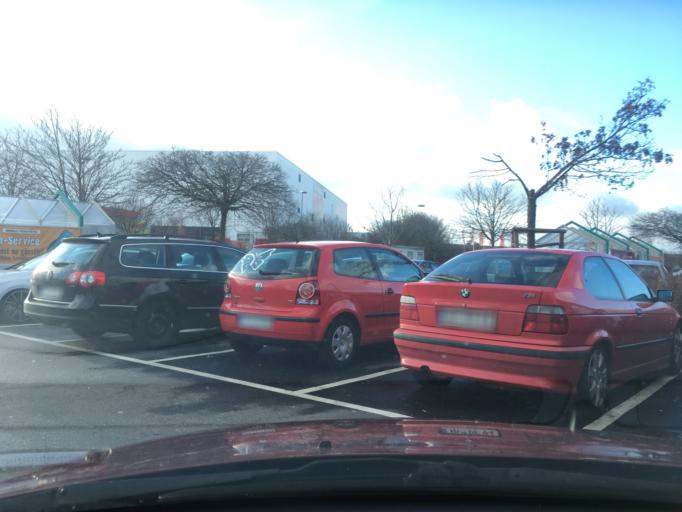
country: DE
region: Saxony
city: Goerlitz
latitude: 51.1904
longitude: 14.9577
